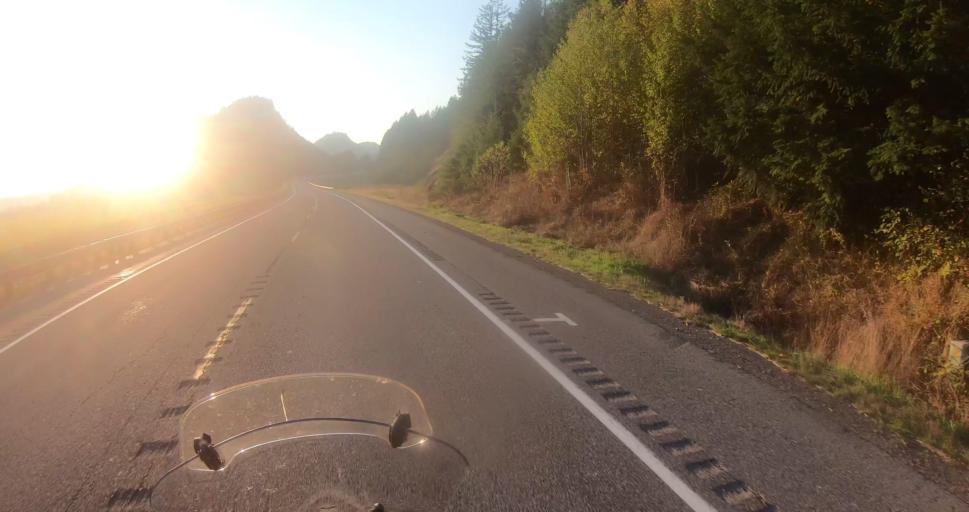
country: US
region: Washington
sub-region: Lewis County
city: Morton
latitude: 46.5363
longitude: -121.9693
